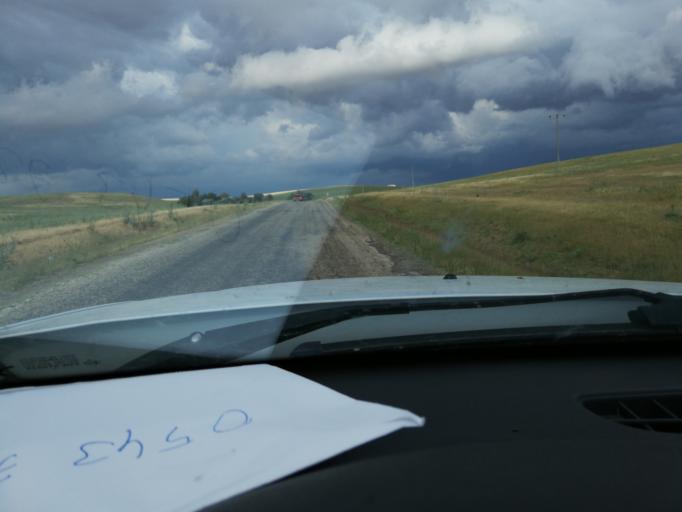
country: TR
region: Kirsehir
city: Kirsehir
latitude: 39.0429
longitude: 34.1594
